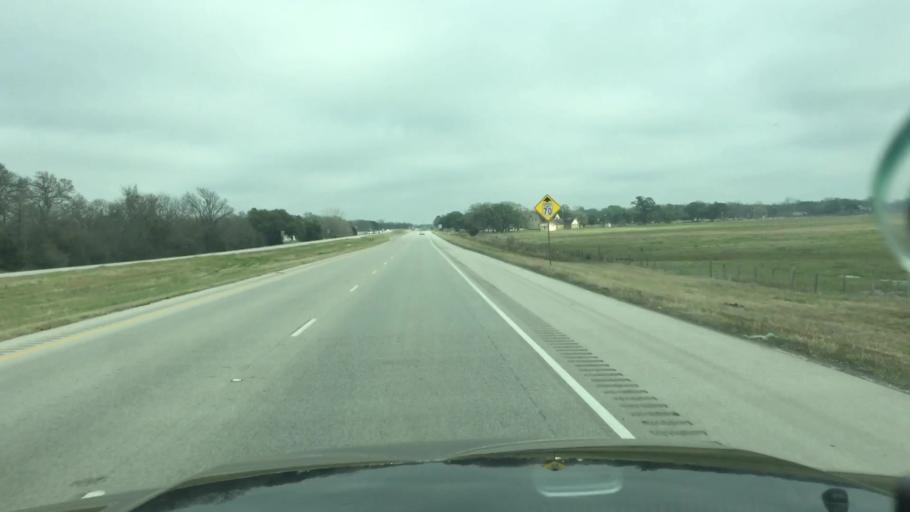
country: US
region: Texas
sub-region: Lee County
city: Giddings
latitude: 30.1481
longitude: -96.6980
